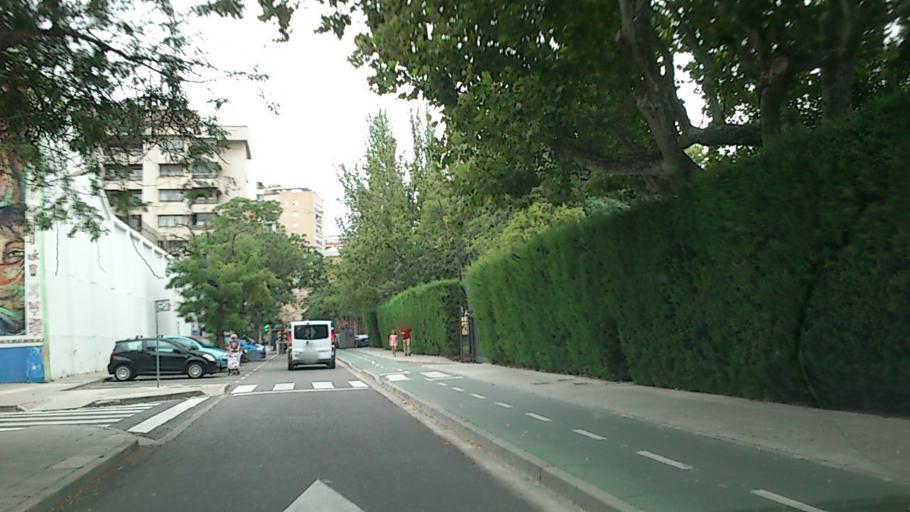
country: ES
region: Aragon
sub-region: Provincia de Zaragoza
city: Delicias
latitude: 41.6415
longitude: -0.9012
